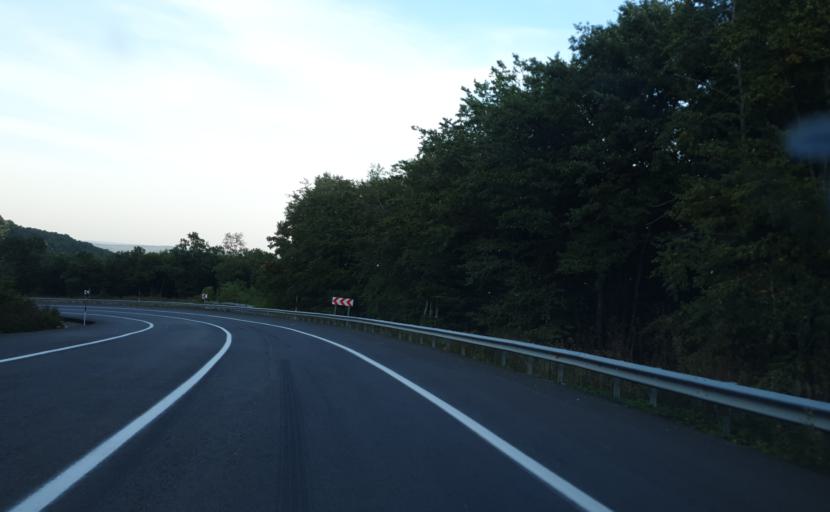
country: TR
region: Kirklareli
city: Sergen
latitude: 41.8040
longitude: 27.7383
